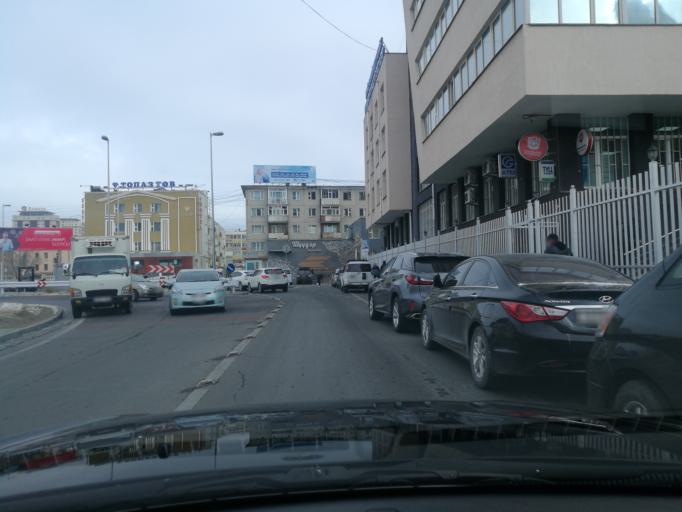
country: MN
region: Ulaanbaatar
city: Ulaanbaatar
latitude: 47.9104
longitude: 106.8955
